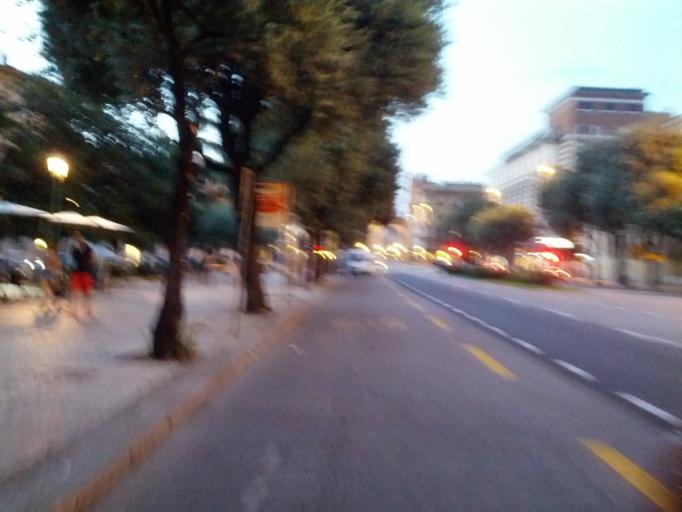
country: IT
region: Veneto
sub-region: Provincia di Verona
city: Verona
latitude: 45.4360
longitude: 10.9903
